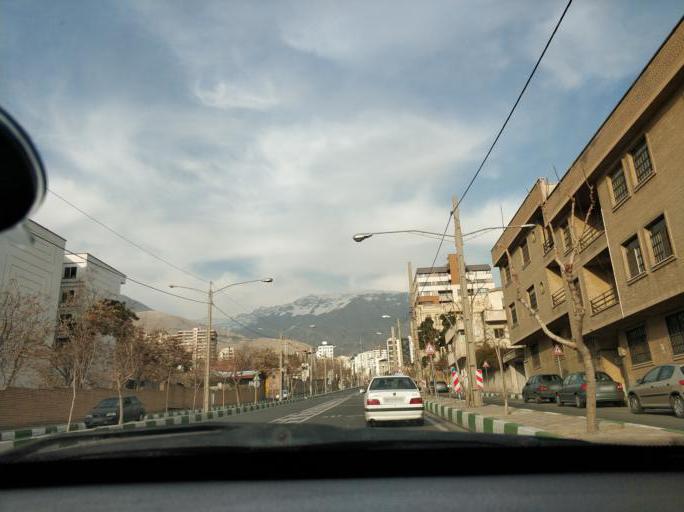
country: IR
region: Tehran
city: Tajrish
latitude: 35.8023
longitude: 51.4810
